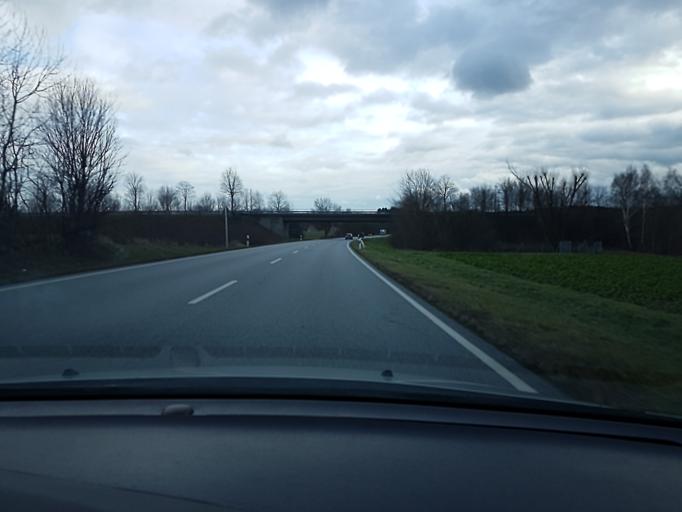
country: DE
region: Bavaria
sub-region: Lower Bavaria
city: Geisenhausen
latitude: 48.4823
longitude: 12.2646
